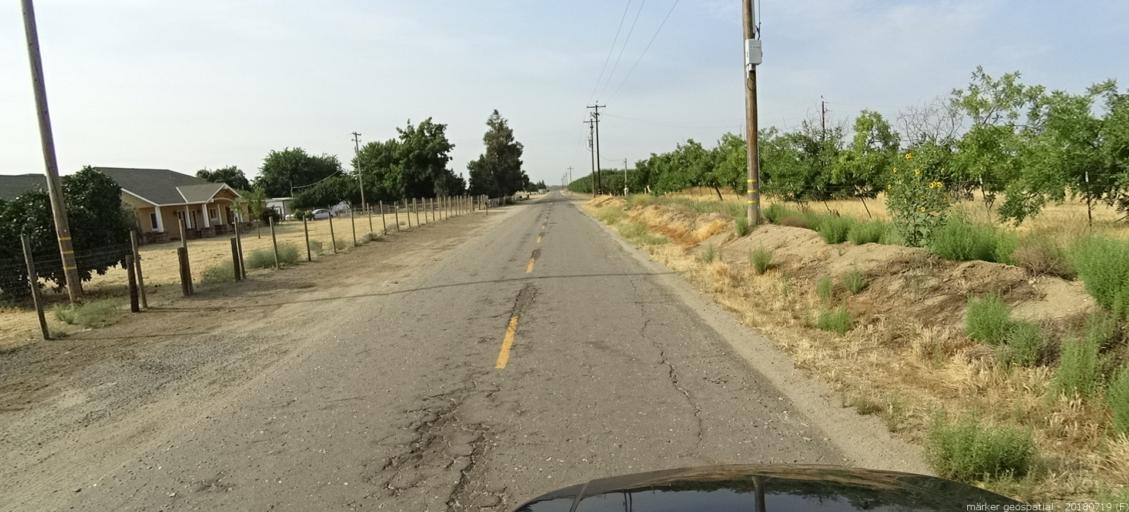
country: US
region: California
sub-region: Madera County
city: Fairmead
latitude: 37.1026
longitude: -120.2113
